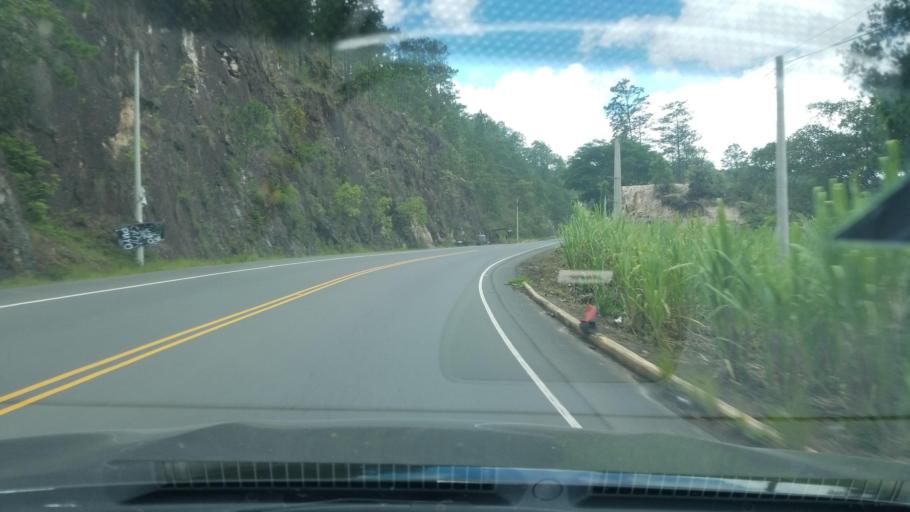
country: HN
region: Francisco Morazan
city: Talanga
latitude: 14.3603
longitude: -87.1429
